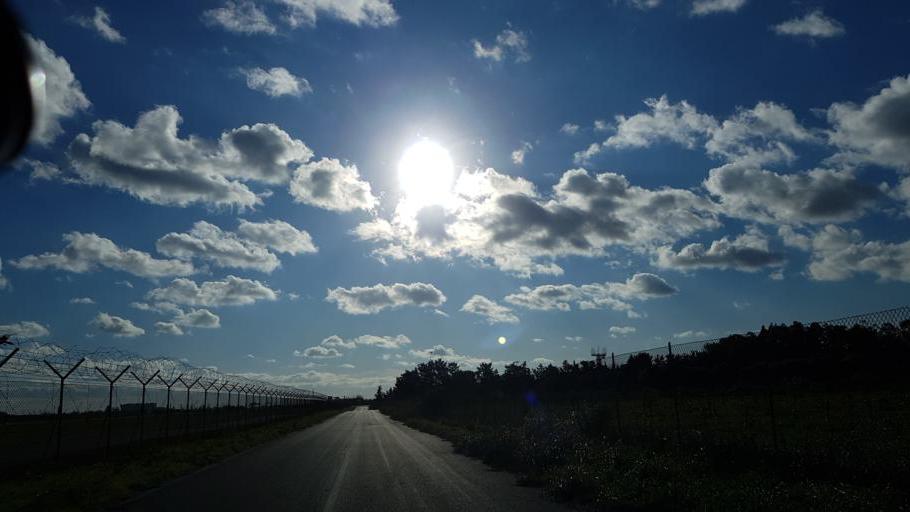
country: IT
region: Apulia
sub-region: Provincia di Brindisi
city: Materdomini
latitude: 40.6631
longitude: 17.9382
